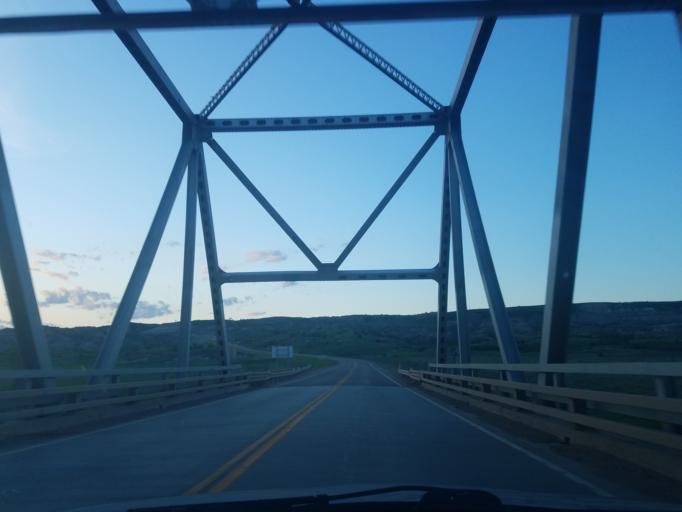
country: US
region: North Dakota
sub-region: McKenzie County
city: Watford City
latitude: 47.5915
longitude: -103.2528
